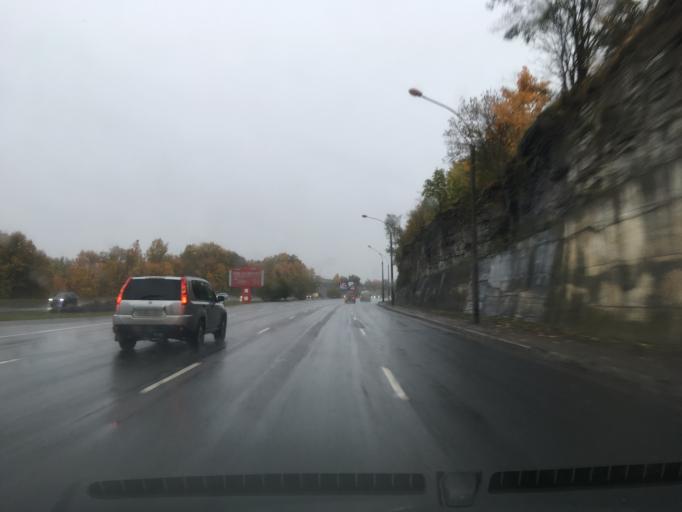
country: EE
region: Harju
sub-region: Tallinna linn
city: Tallinn
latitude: 59.4341
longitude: 24.7911
